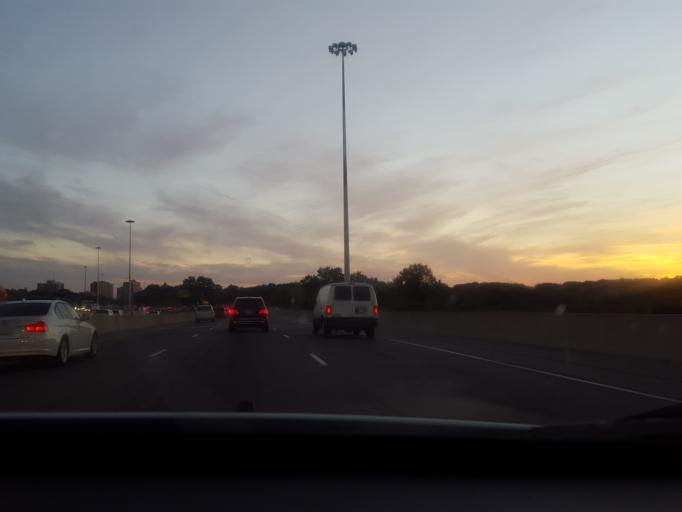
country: CA
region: Ontario
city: North York
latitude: 43.7510
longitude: -79.4127
